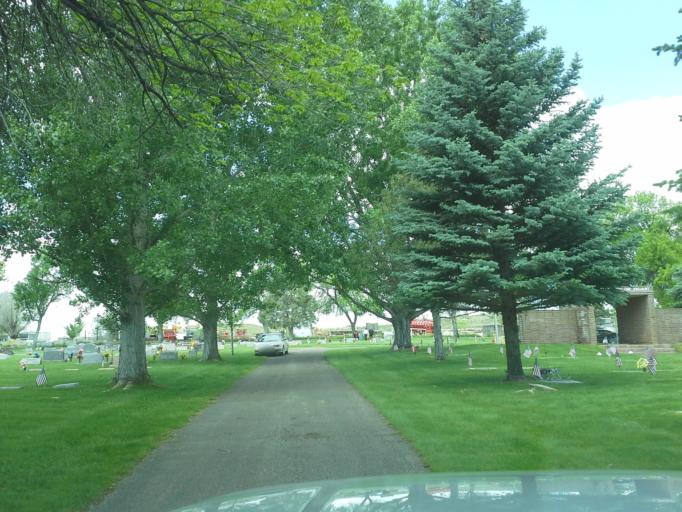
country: US
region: Wyoming
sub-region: Washakie County
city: Worland
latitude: 44.0228
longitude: -107.9754
